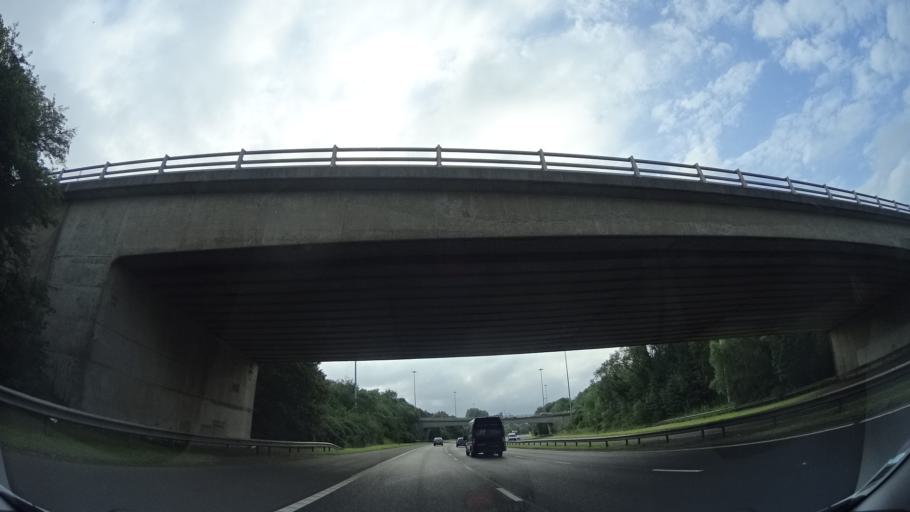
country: GB
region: England
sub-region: Knowsley
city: Huyton
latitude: 53.4080
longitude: -2.8687
